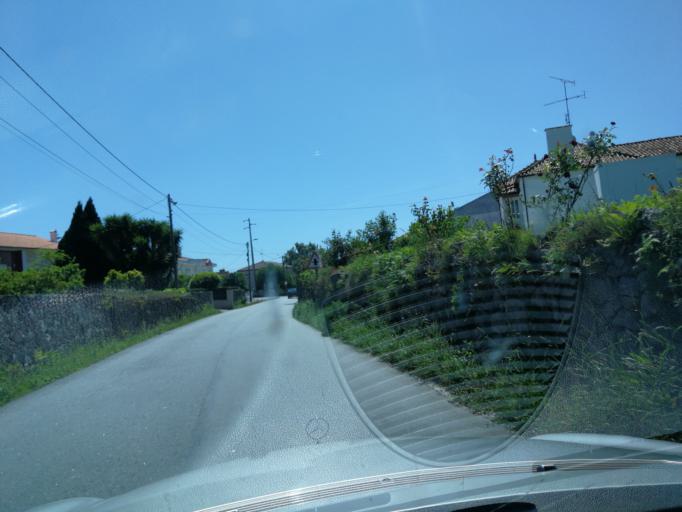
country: PT
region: Viana do Castelo
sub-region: Viana do Castelo
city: Meadela
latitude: 41.7161
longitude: -8.7989
